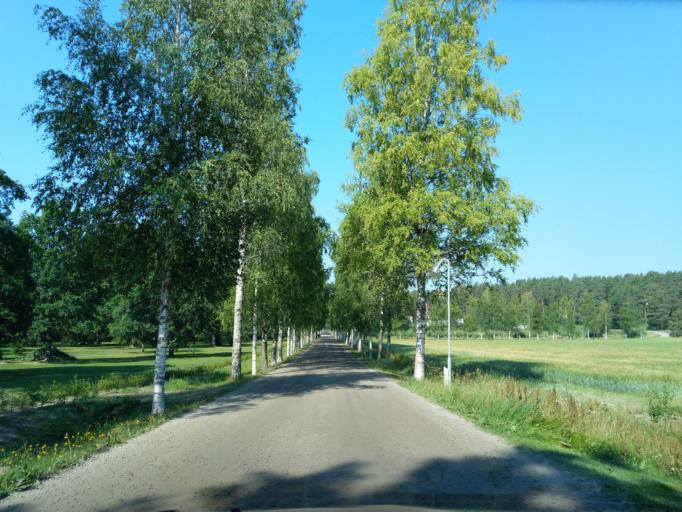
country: FI
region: Satakunta
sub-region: Pori
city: Noormarkku
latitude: 61.5947
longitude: 21.8817
